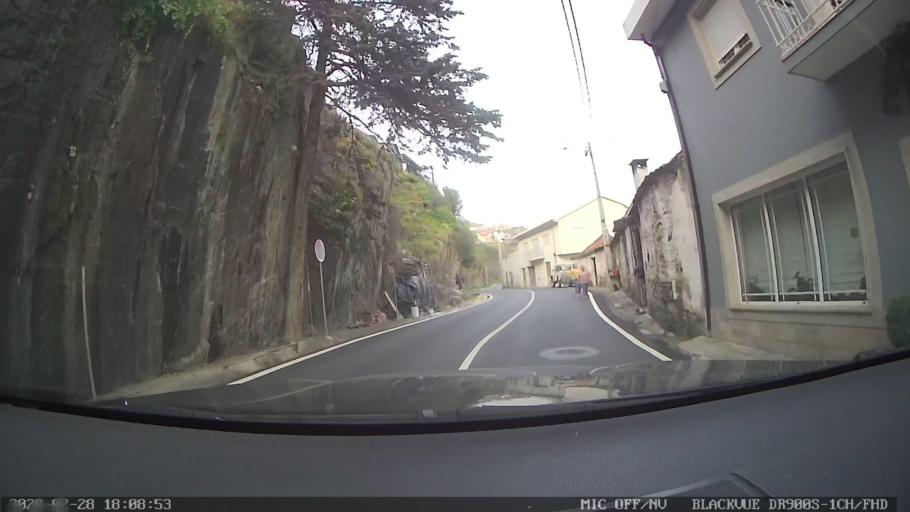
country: PT
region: Vila Real
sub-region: Sabrosa
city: Vilela
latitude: 41.1939
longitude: -7.5495
